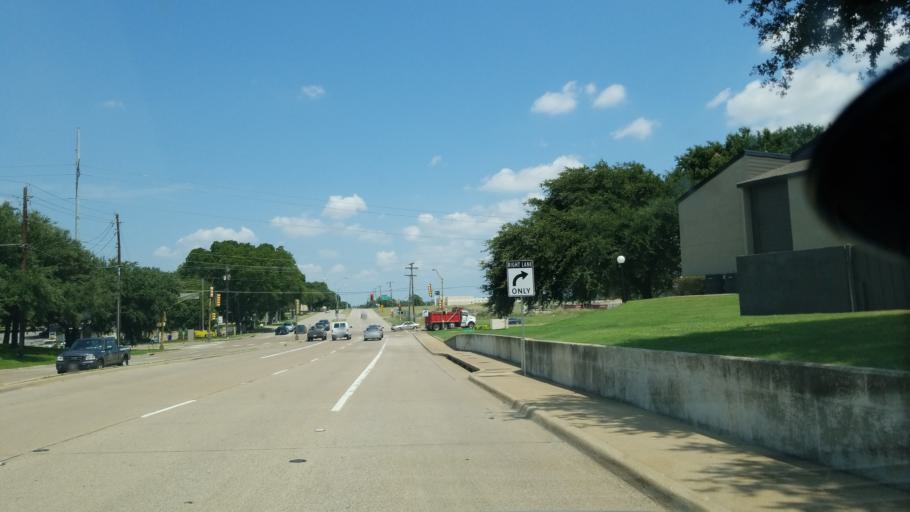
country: US
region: Texas
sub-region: Dallas County
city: Richardson
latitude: 32.9222
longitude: -96.7406
